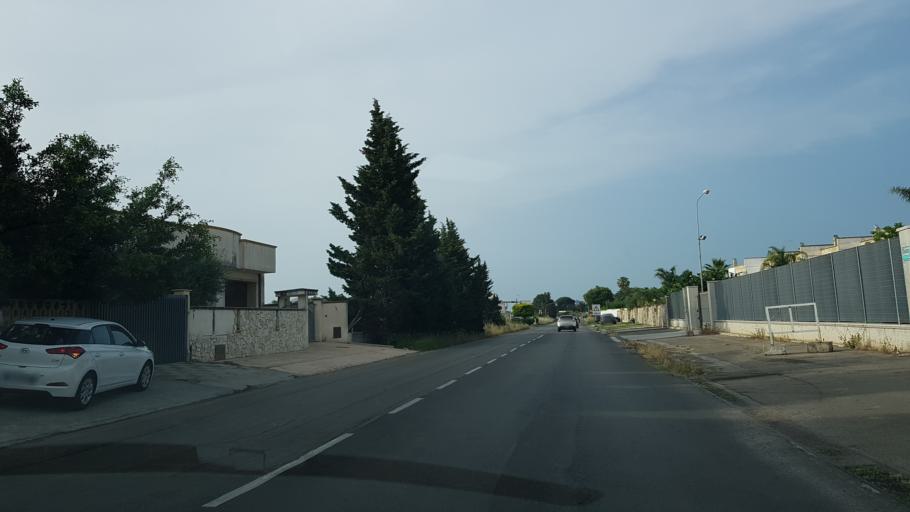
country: IT
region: Apulia
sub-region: Provincia di Brindisi
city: San Pietro Vernotico
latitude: 40.4953
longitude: 17.9913
